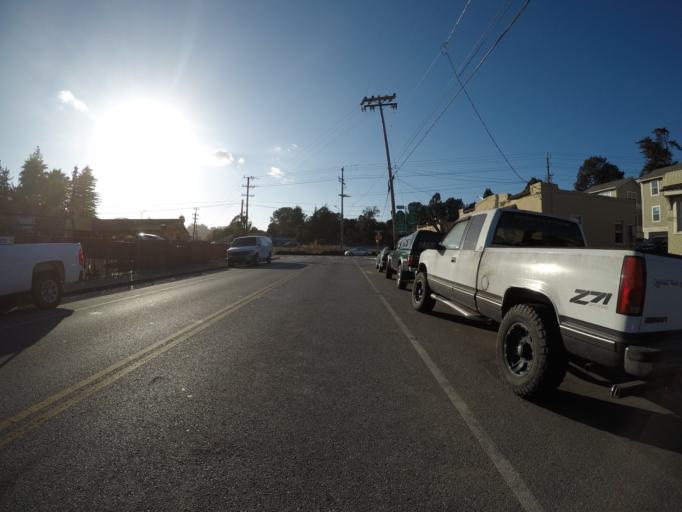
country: US
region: California
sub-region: Santa Cruz County
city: Santa Cruz
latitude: 36.9857
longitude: -122.0225
